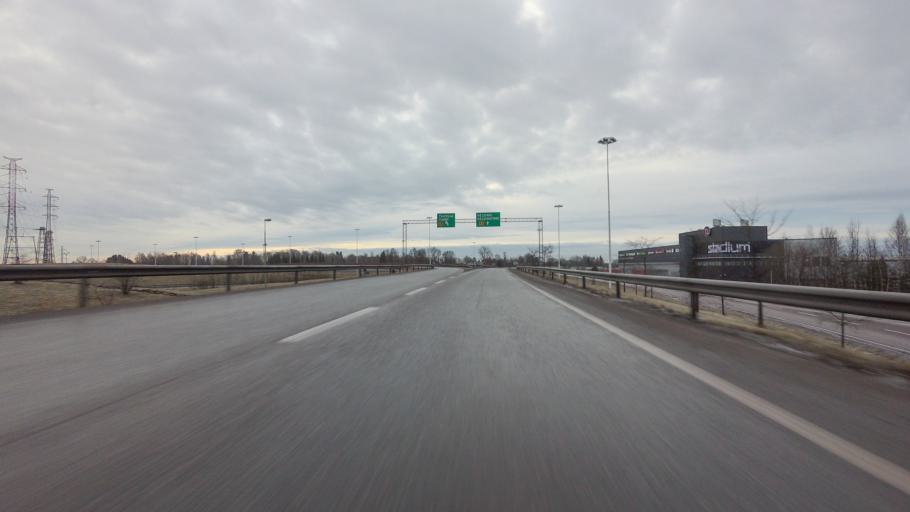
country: FI
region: Uusimaa
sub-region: Helsinki
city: Vantaa
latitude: 60.2874
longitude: 24.9775
